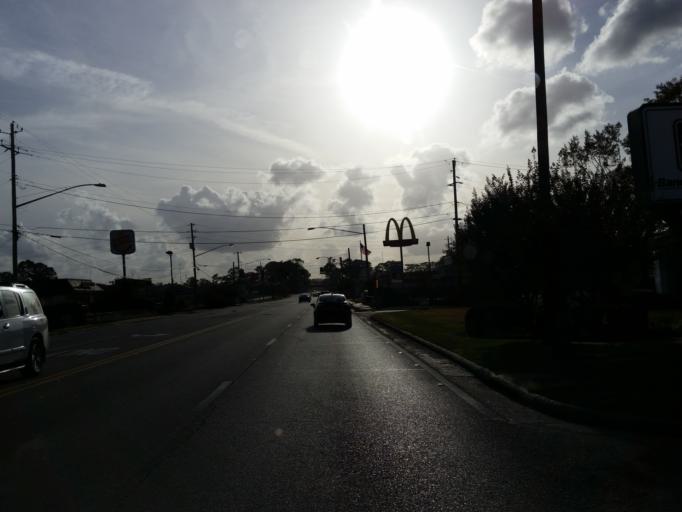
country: US
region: Mississippi
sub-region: Forrest County
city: Hattiesburg
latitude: 31.3121
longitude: -89.3113
